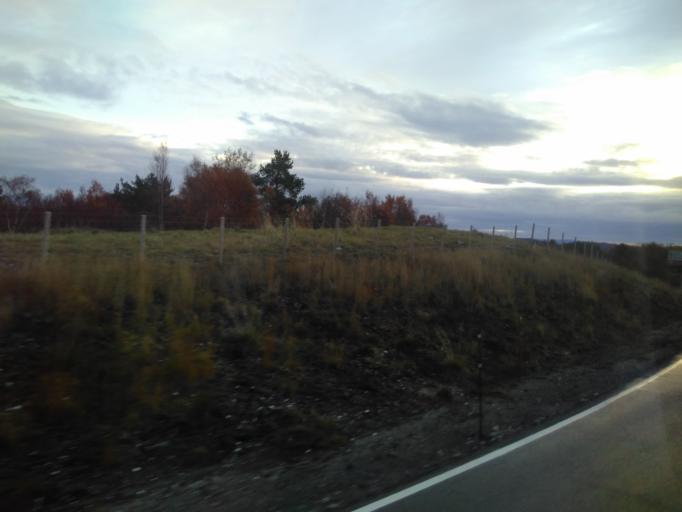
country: NO
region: Sor-Trondelag
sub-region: Froya
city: Sistranda
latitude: 63.6360
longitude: 8.8275
